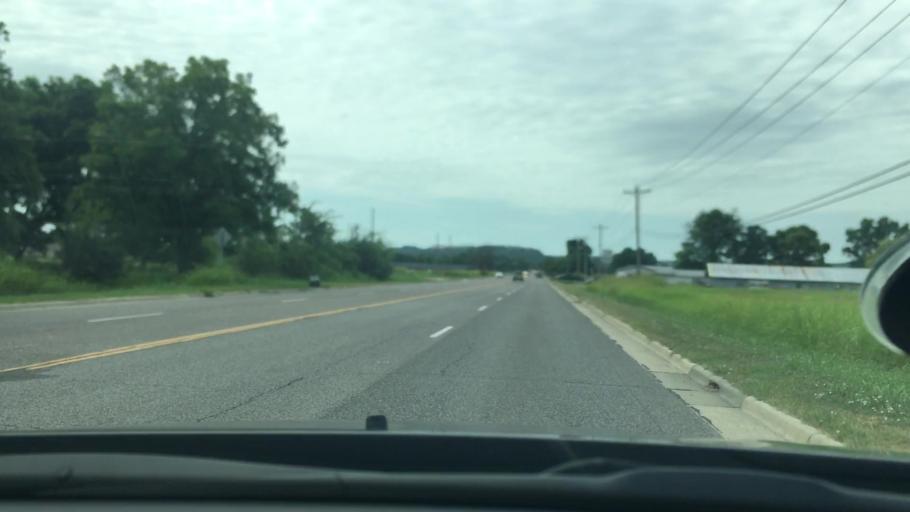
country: US
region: Oklahoma
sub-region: Murray County
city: Davis
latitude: 34.4722
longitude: -97.1316
